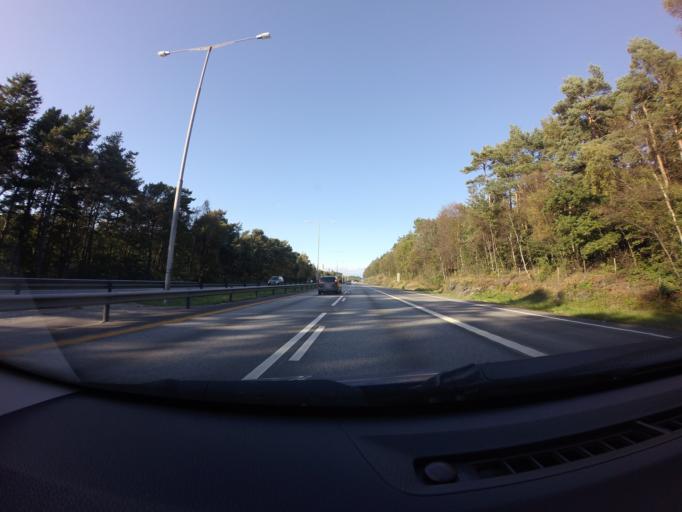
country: NO
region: Rogaland
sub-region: Stavanger
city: Stavanger
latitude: 58.9247
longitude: 5.7077
